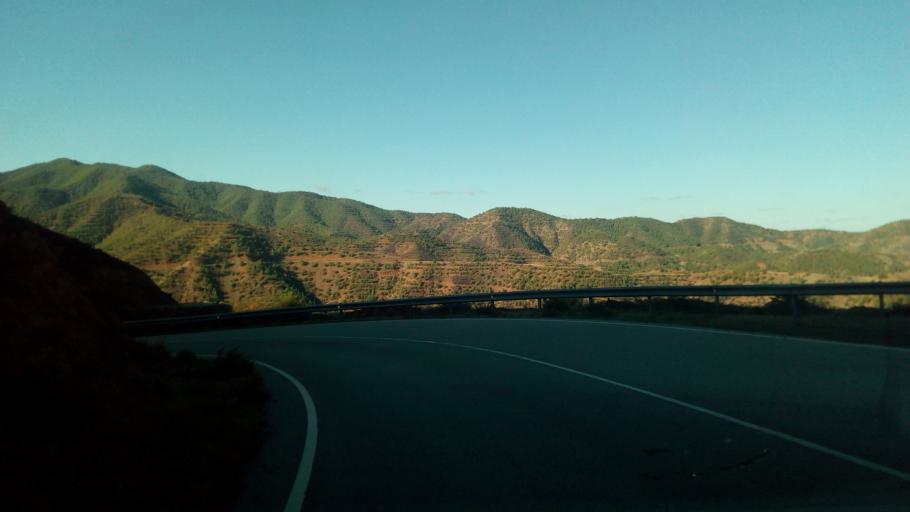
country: CY
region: Lefkosia
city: Lefka
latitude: 35.1073
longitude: 32.7715
